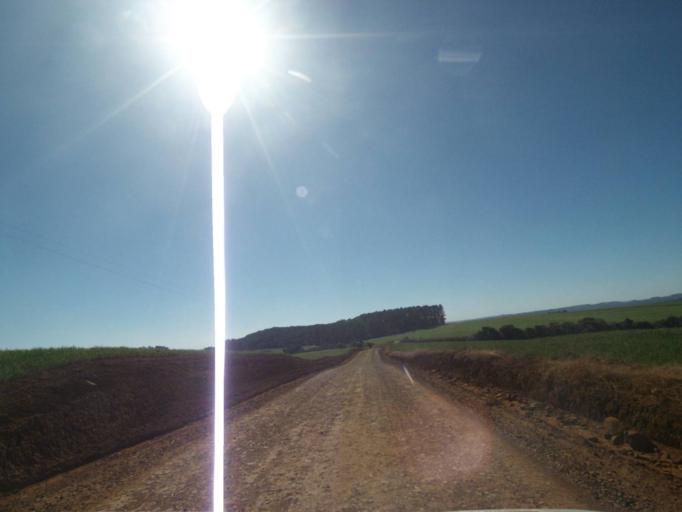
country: BR
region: Parana
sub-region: Tibagi
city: Tibagi
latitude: -24.6024
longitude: -50.6034
